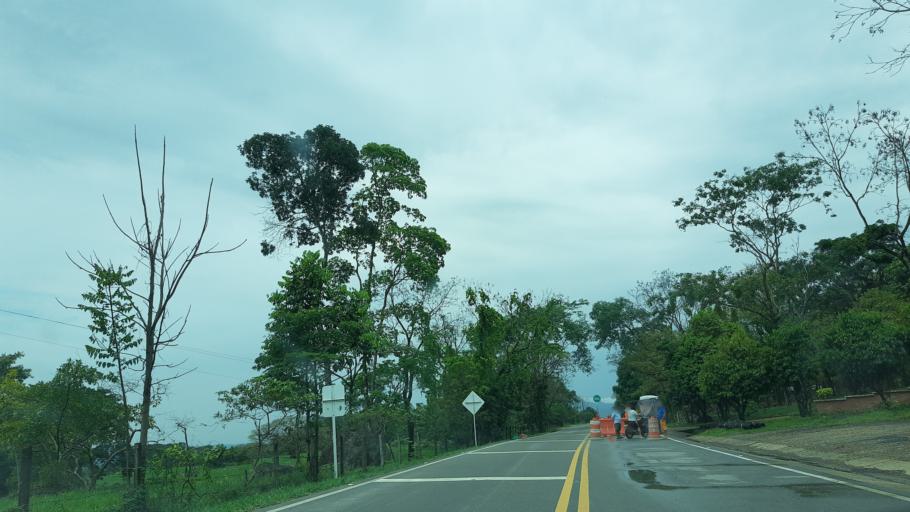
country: CO
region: Casanare
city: Monterrey
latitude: 4.8345
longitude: -72.9577
